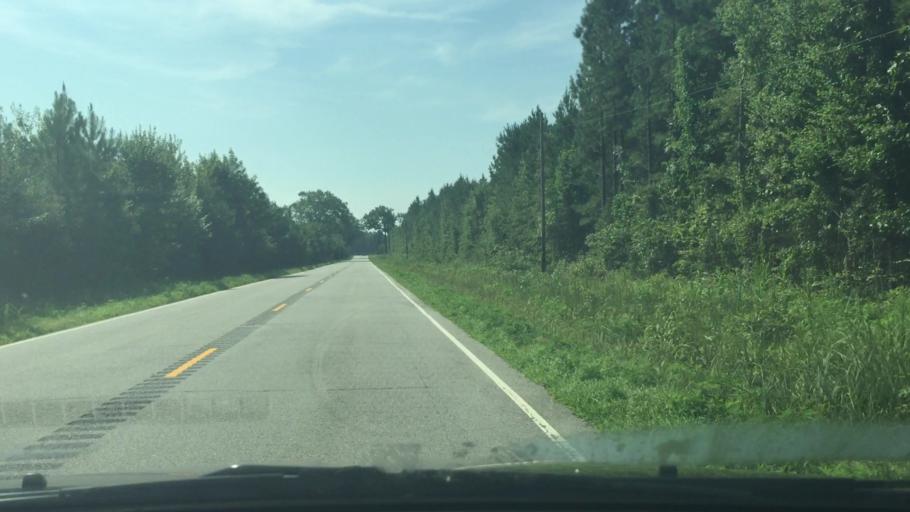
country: US
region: Virginia
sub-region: Sussex County
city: Sussex
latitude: 36.8624
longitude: -77.1386
